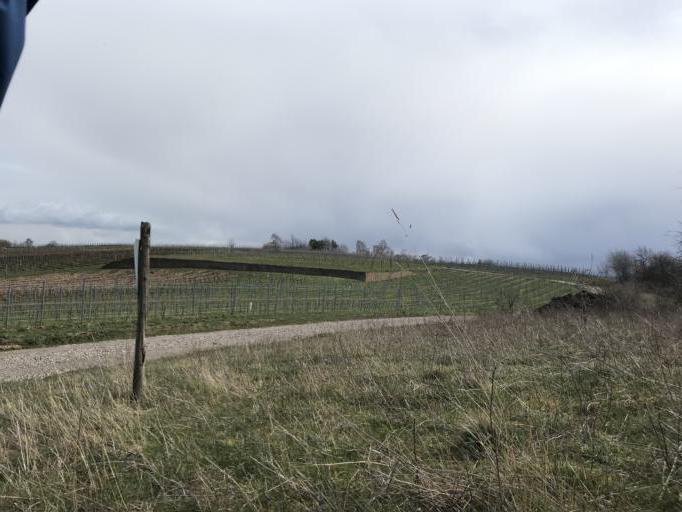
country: DE
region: Rheinland-Pfalz
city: Siefersheim
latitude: 49.7917
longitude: 7.9366
